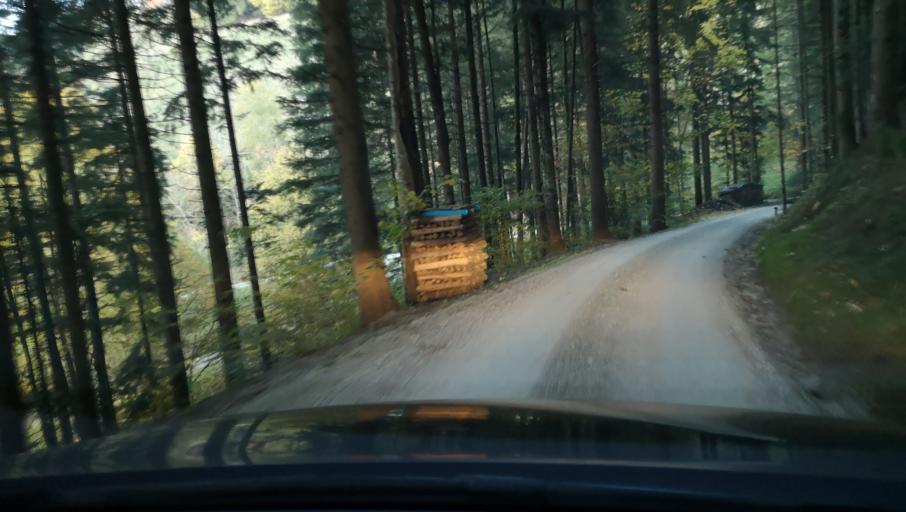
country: AT
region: Styria
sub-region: Politischer Bezirk Weiz
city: Birkfeld
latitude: 47.3672
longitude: 15.6564
